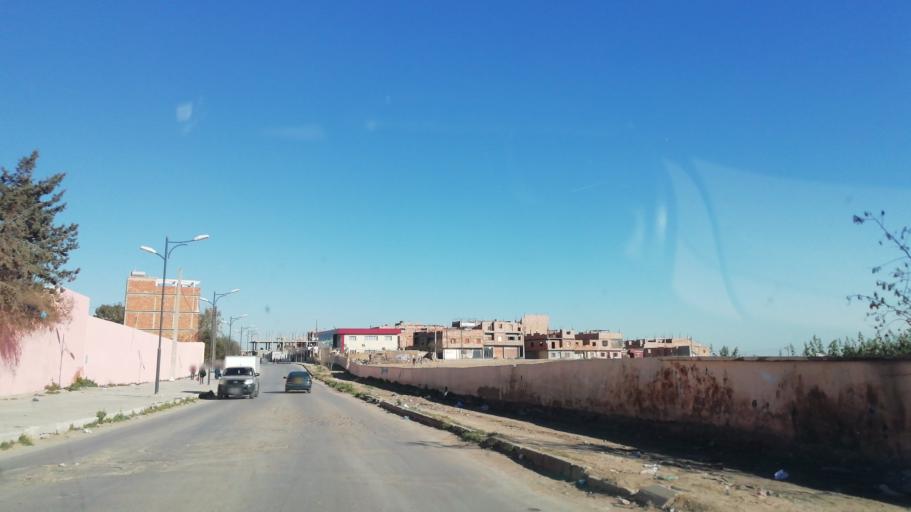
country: DZ
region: Oran
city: Bir el Djir
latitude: 35.7242
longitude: -0.5326
